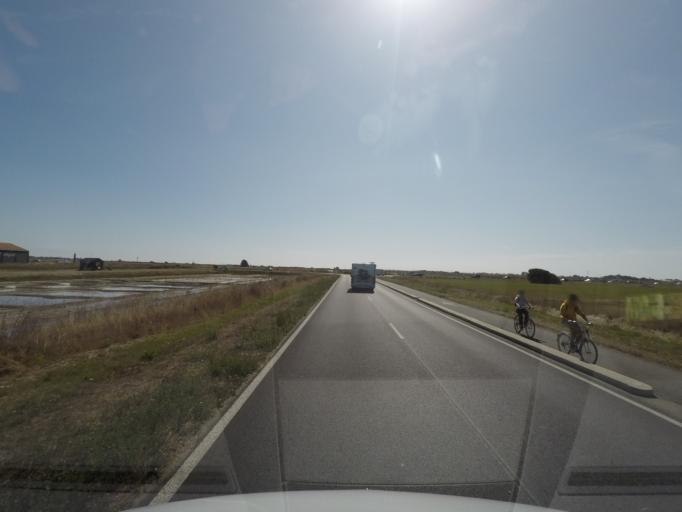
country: FR
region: Pays de la Loire
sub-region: Departement de la Vendee
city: La Gueriniere
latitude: 46.9901
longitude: -2.2500
